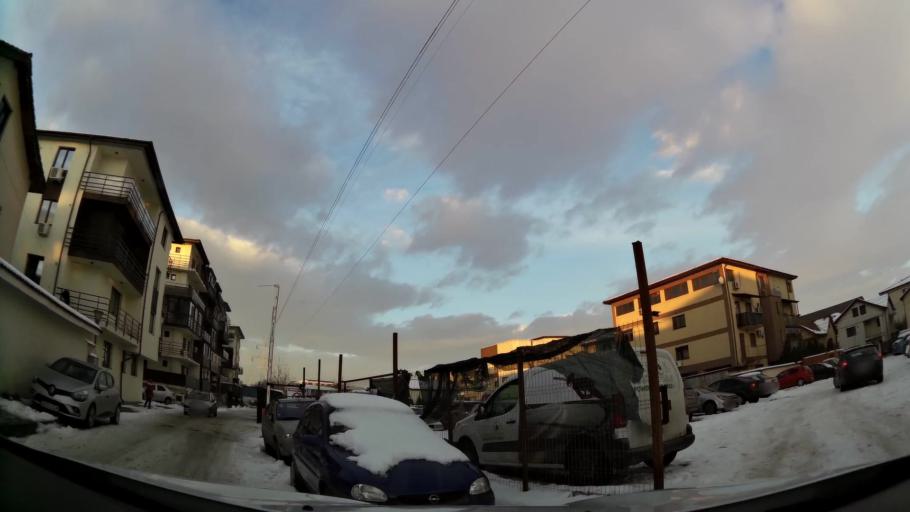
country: RO
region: Ilfov
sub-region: Comuna Popesti-Leordeni
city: Popesti-Leordeni
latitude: 44.3749
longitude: 26.1472
